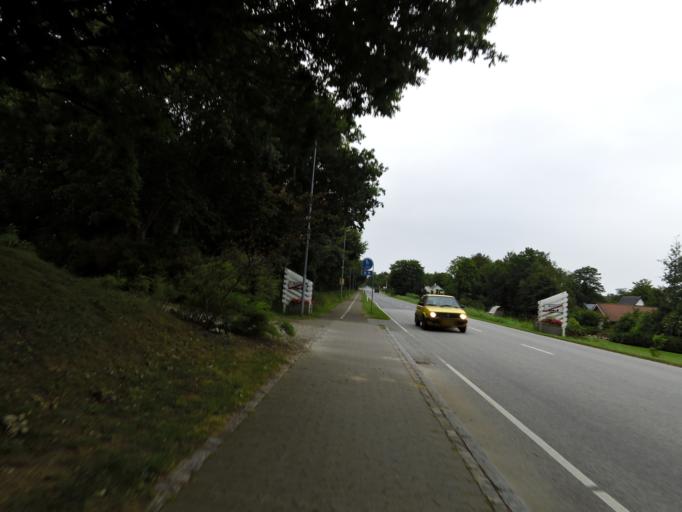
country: DK
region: South Denmark
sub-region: Tonder Kommune
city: Logumkloster
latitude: 55.1523
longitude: 8.9608
